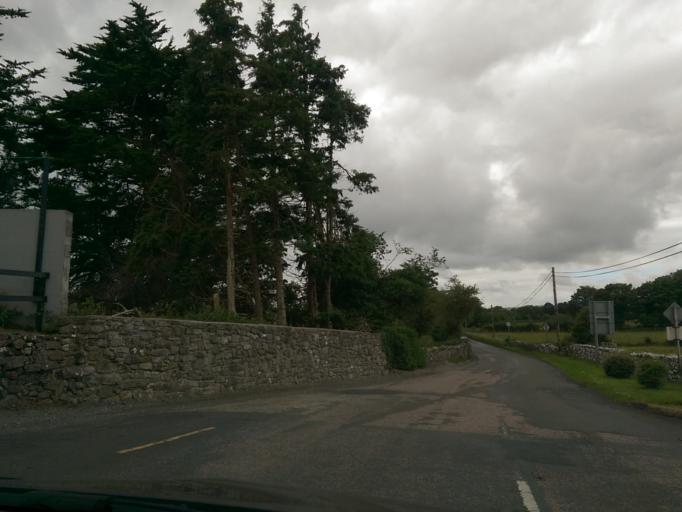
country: IE
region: Connaught
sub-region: County Galway
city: Loughrea
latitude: 53.2475
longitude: -8.5544
